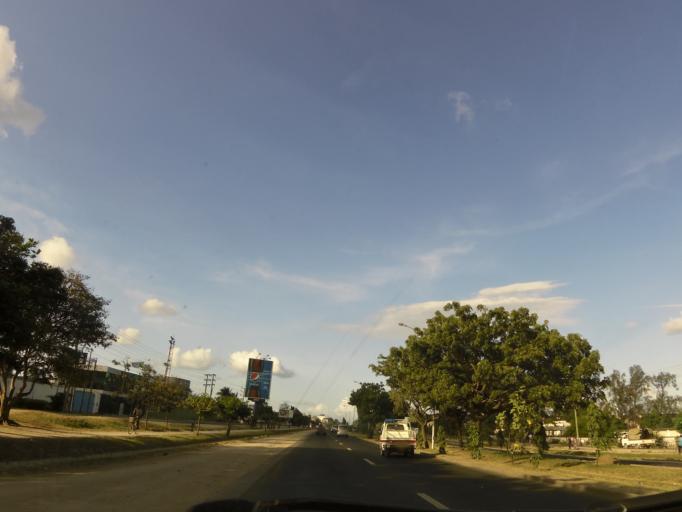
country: TZ
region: Dar es Salaam
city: Dar es Salaam
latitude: -6.8494
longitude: 39.2343
